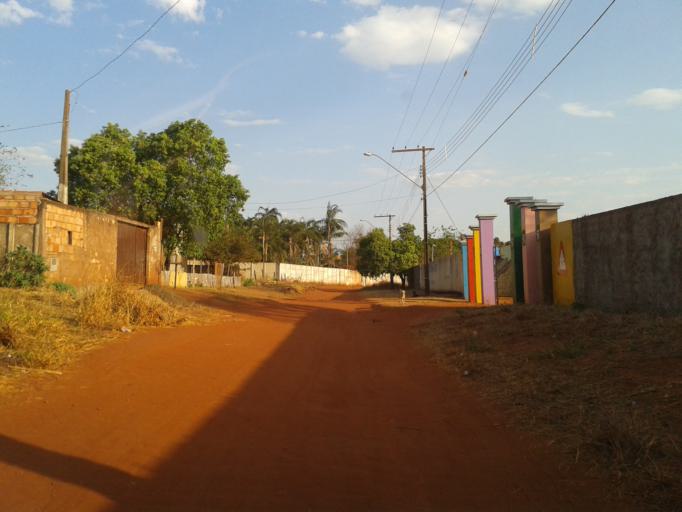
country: BR
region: Minas Gerais
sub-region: Ituiutaba
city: Ituiutaba
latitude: -18.9964
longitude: -49.4364
